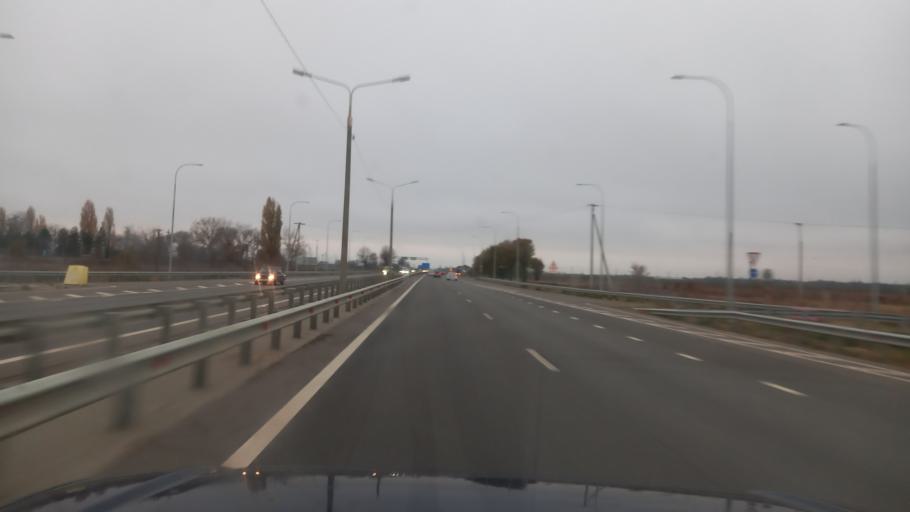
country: RU
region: Adygeya
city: Maykop
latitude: 44.6314
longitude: 40.0410
